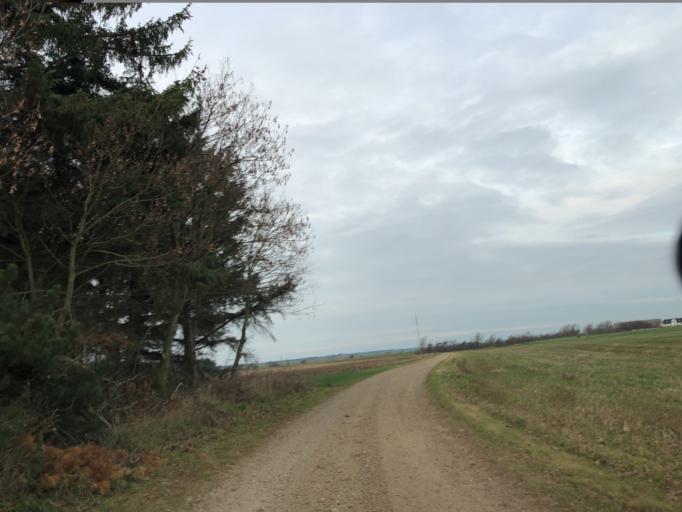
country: DK
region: Central Jutland
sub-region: Holstebro Kommune
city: Ulfborg
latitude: 56.2729
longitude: 8.2169
